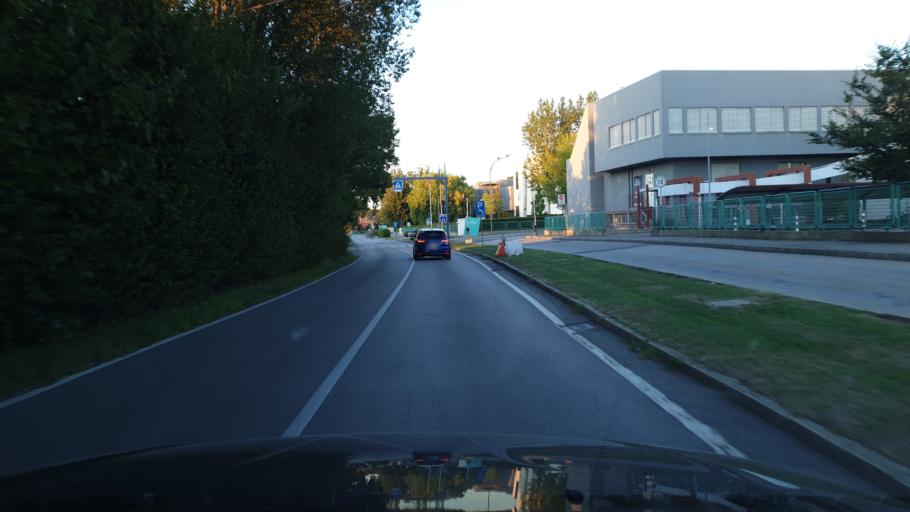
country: IT
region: Emilia-Romagna
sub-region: Provincia di Bologna
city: Quarto Inferiore
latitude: 44.5317
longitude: 11.3871
